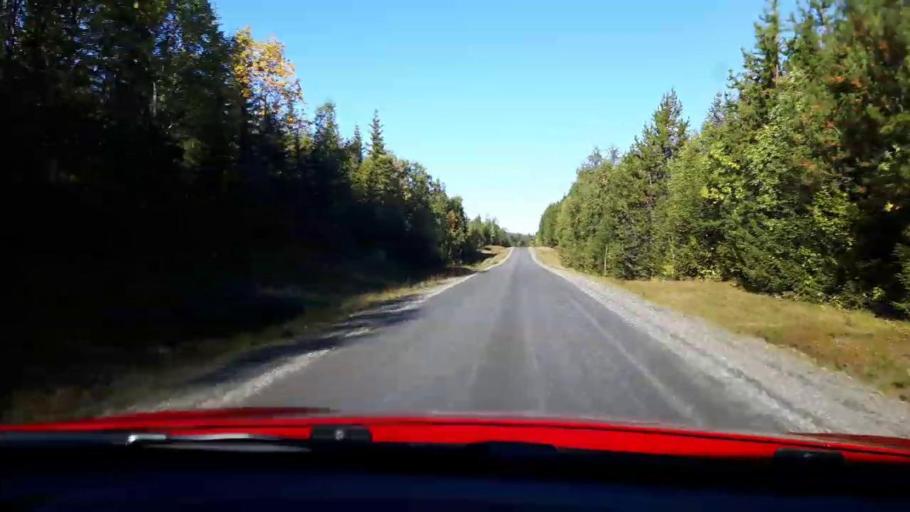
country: NO
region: Nord-Trondelag
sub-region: Lierne
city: Sandvika
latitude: 64.5273
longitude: 14.0550
